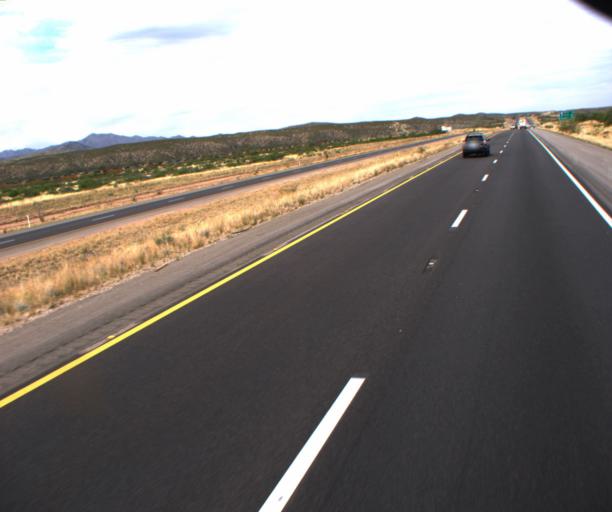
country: US
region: Arizona
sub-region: Cochise County
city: Mescal
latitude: 31.9844
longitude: -110.5539
